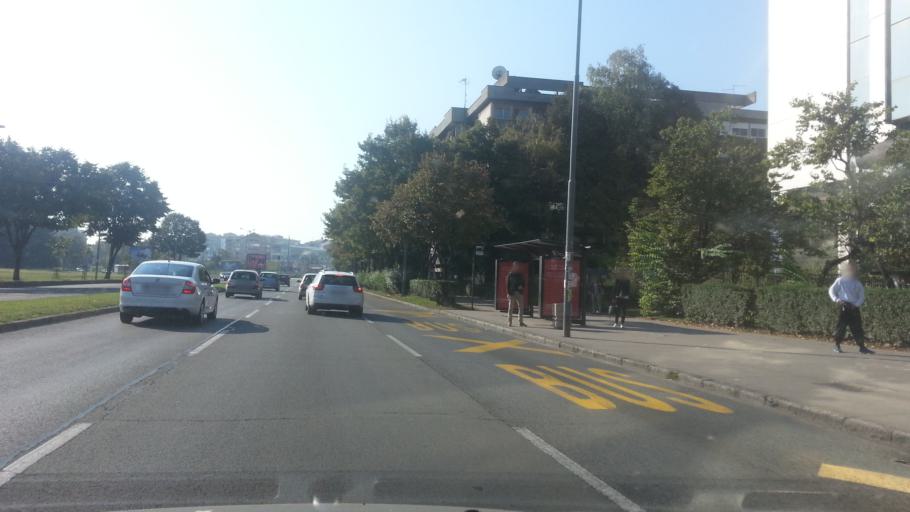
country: RS
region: Central Serbia
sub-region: Belgrade
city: Novi Beograd
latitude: 44.8274
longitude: 20.4196
